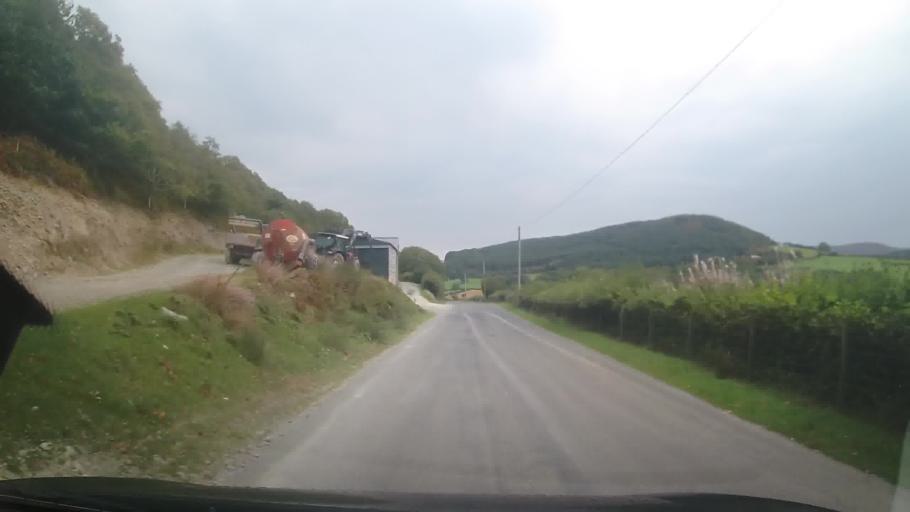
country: GB
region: Wales
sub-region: Sir Powys
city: Rhayader
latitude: 52.3103
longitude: -3.5430
